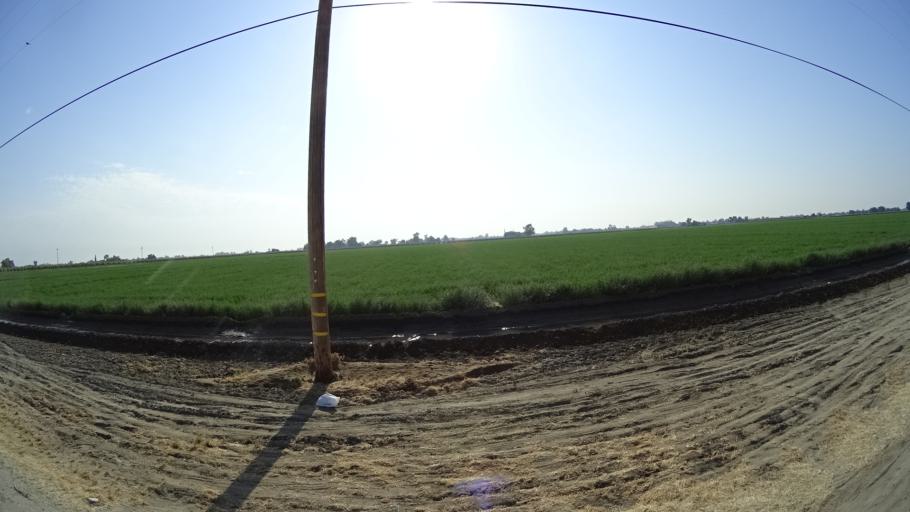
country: US
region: California
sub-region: Fresno County
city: Riverdale
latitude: 36.3713
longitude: -119.8603
